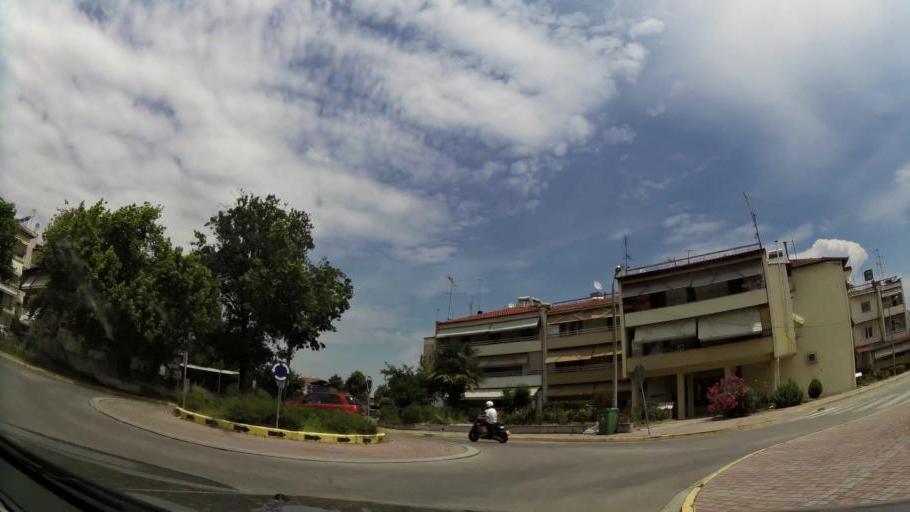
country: GR
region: Central Macedonia
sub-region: Nomos Pierias
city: Katerini
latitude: 40.2727
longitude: 22.5191
